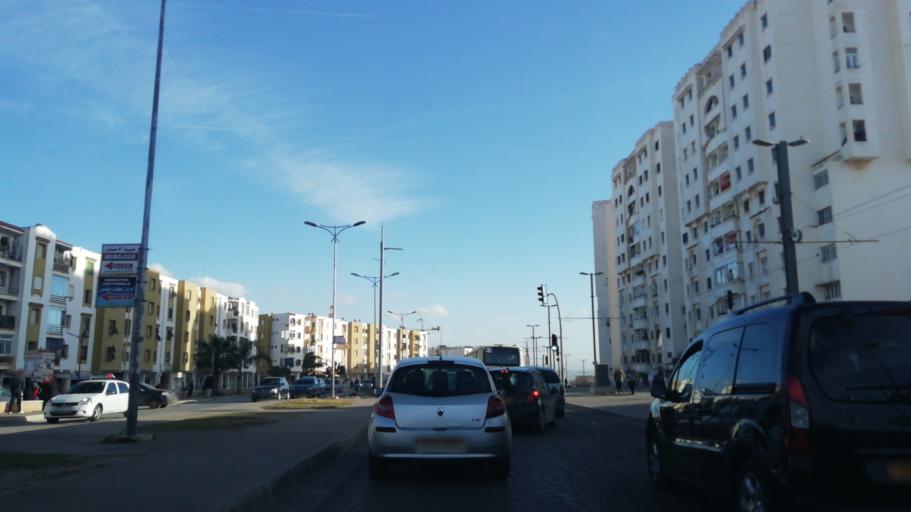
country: DZ
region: Oran
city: Bir el Djir
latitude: 35.7033
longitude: -0.5698
